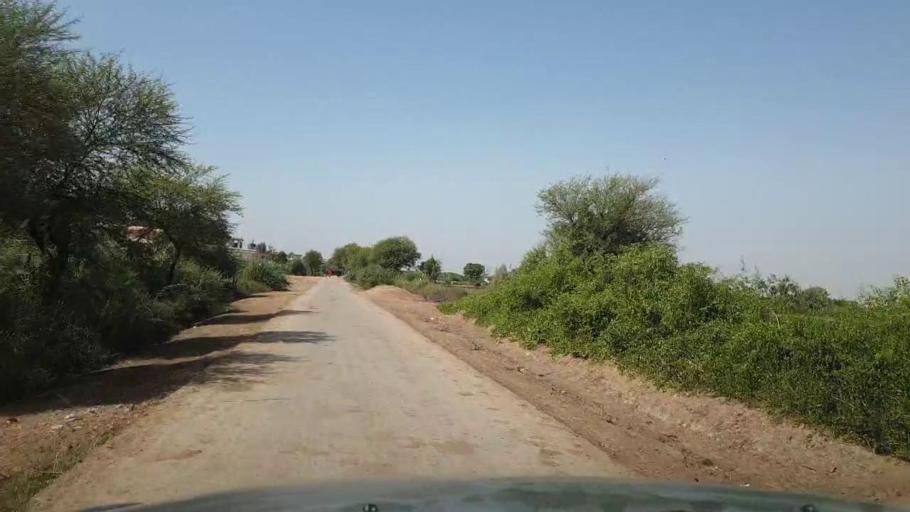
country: PK
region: Sindh
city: Tando Muhammad Khan
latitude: 25.1487
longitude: 68.4401
